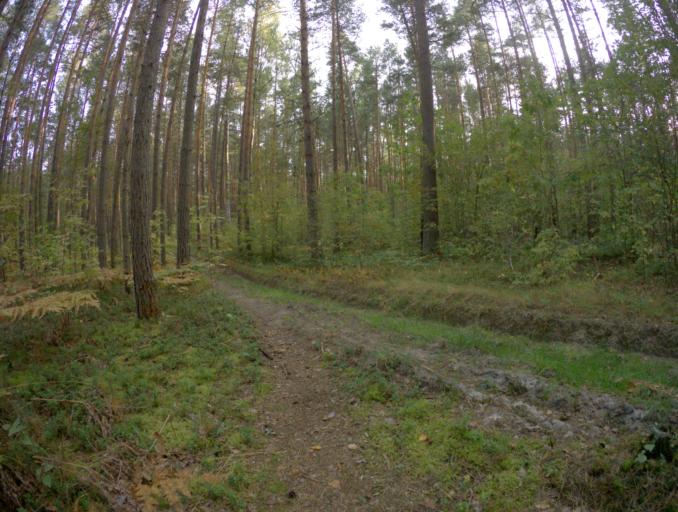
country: RU
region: Vladimir
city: Raduzhnyy
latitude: 56.0560
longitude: 40.3485
